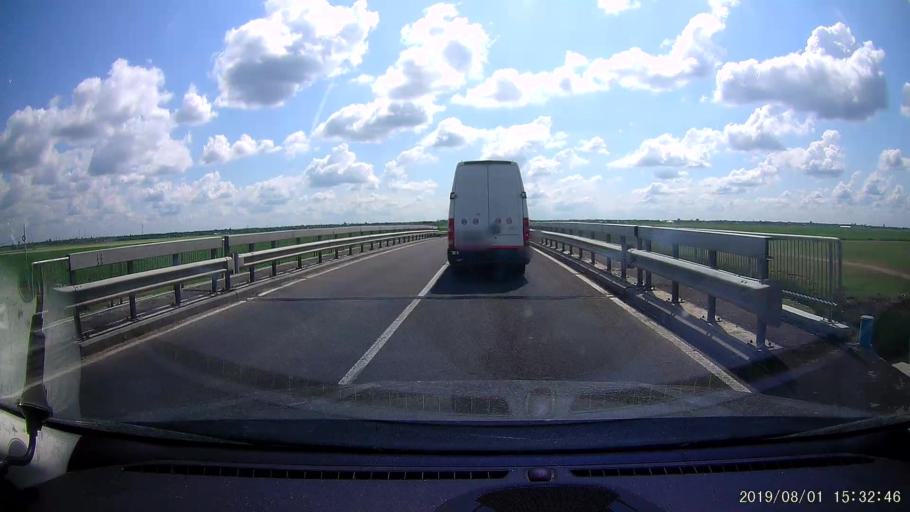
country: RO
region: Braila
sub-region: Comuna Insuratei
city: Insuratei
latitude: 44.9296
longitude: 27.6326
